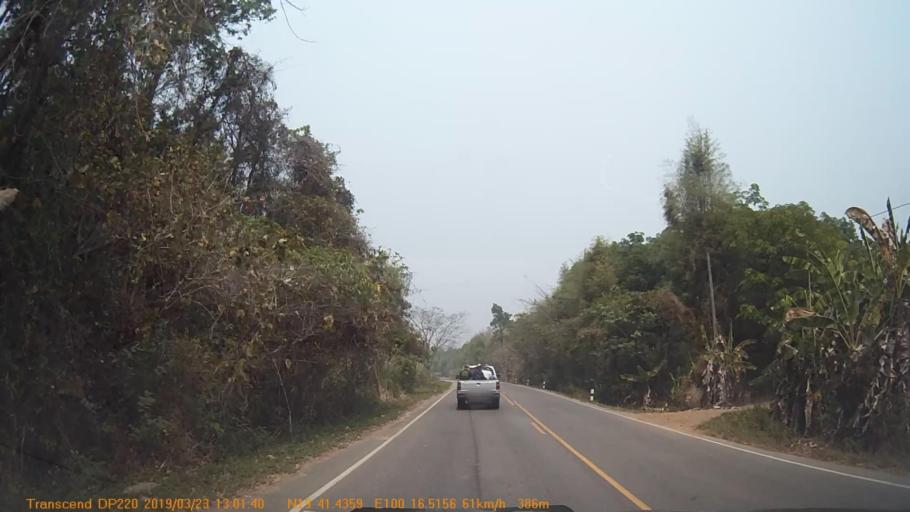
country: TH
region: Chiang Rai
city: Thoeng
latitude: 19.6909
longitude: 100.2754
